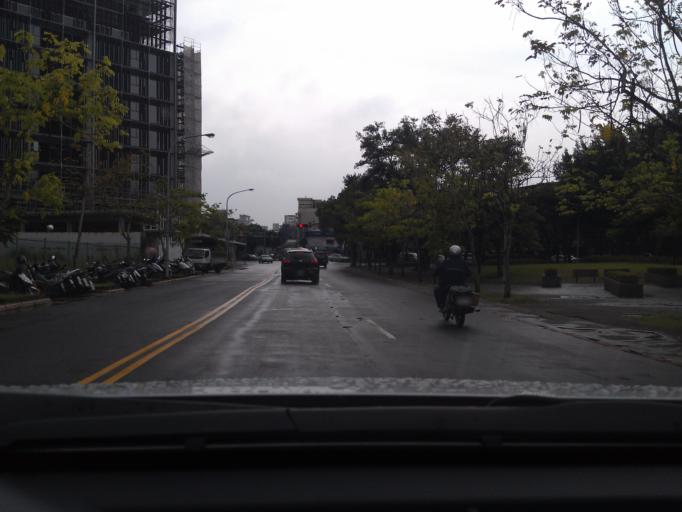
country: TW
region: Taipei
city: Taipei
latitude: 25.0946
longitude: 121.5292
